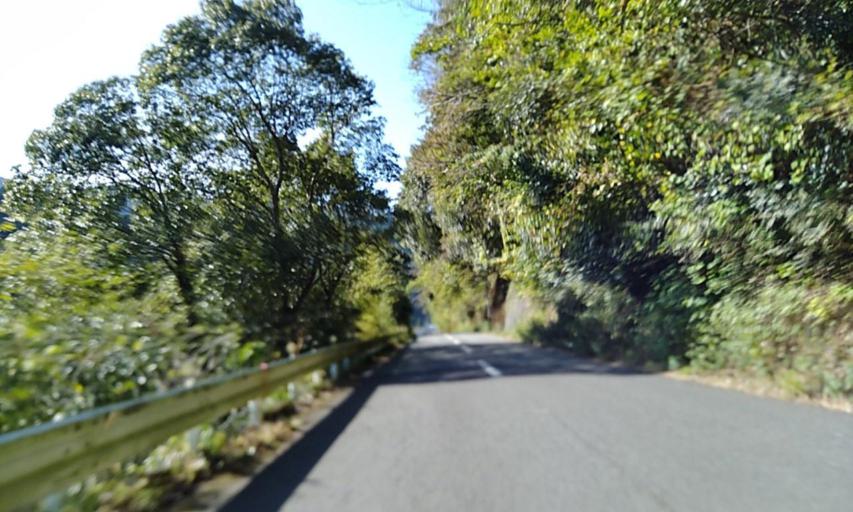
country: JP
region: Wakayama
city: Kainan
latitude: 34.0553
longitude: 135.3306
